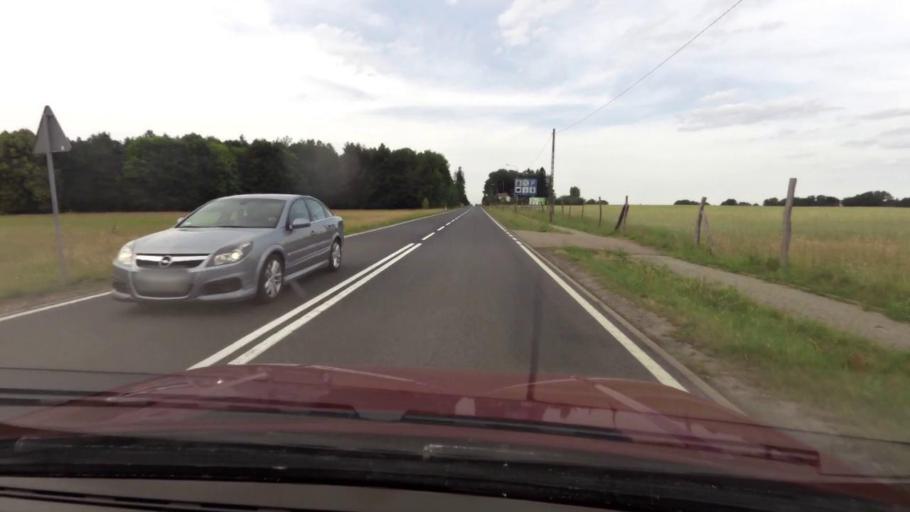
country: PL
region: Pomeranian Voivodeship
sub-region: Powiat bytowski
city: Trzebielino
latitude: 54.2414
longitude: 17.0950
